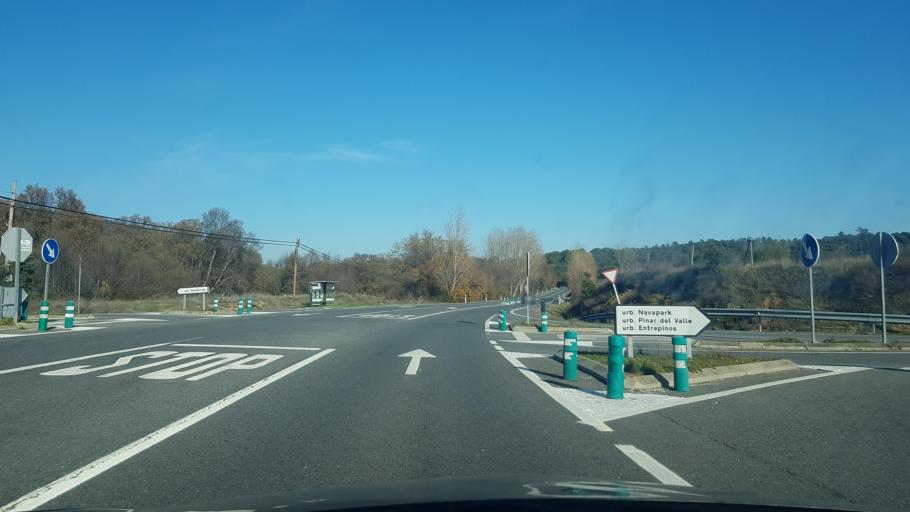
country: ES
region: Madrid
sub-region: Provincia de Madrid
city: Rozas de Puerto Real
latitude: 40.3341
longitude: -4.4674
